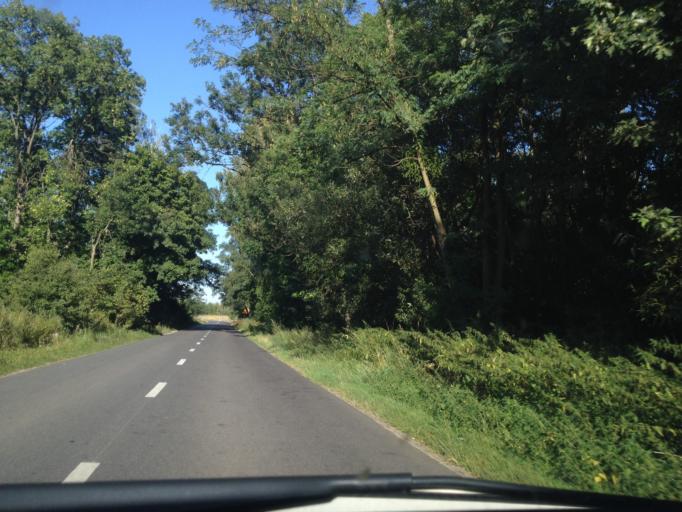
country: PL
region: Greater Poland Voivodeship
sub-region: Powiat sremski
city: Srem
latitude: 52.1073
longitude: 17.0662
